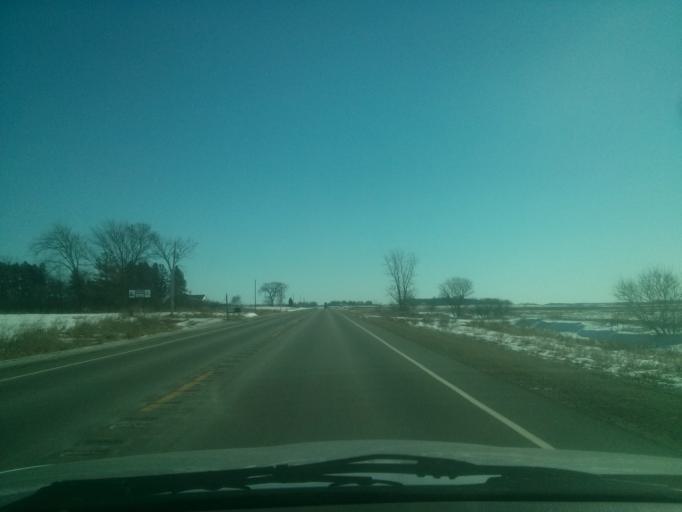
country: US
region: Wisconsin
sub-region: Polk County
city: Clear Lake
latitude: 45.1365
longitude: -92.3701
